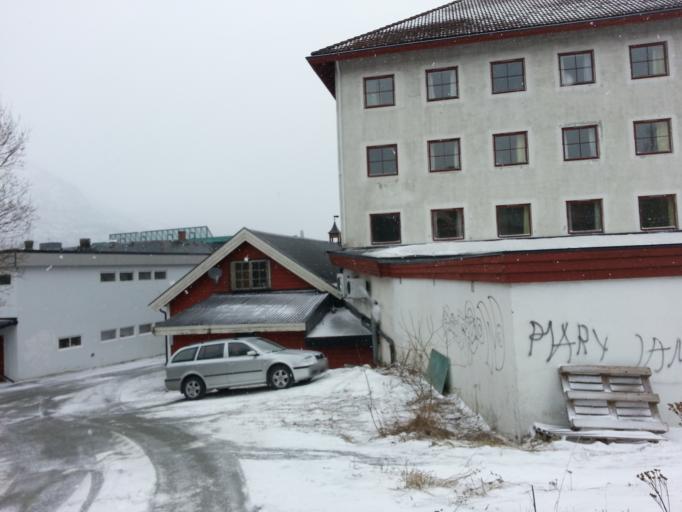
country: NO
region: Sor-Trondelag
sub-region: Oppdal
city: Oppdal
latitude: 62.5961
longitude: 9.6923
